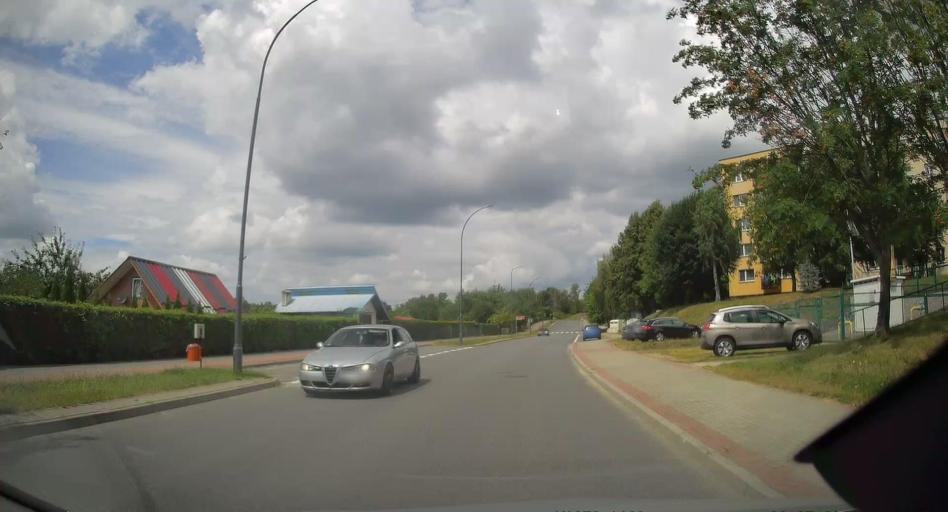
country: PL
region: Subcarpathian Voivodeship
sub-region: Powiat ropczycko-sedziszowski
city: Ropczyce
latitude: 50.0577
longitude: 21.5997
